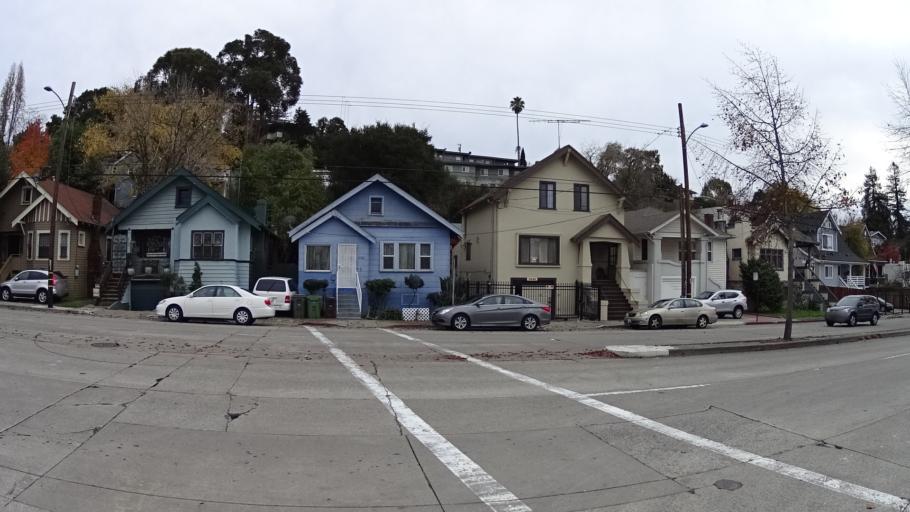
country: US
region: California
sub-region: Alameda County
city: Piedmont
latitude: 37.7962
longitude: -122.2345
